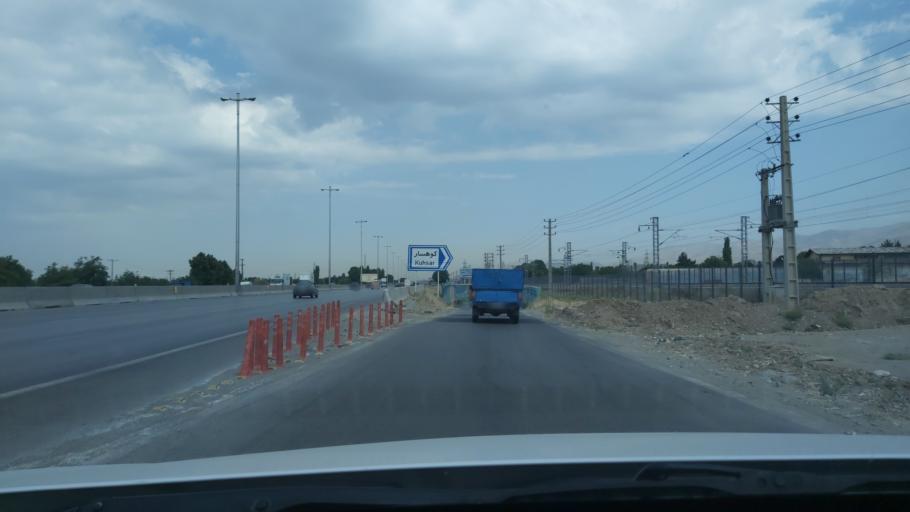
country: IR
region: Alborz
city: Hashtgerd
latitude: 35.9335
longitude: 50.7587
